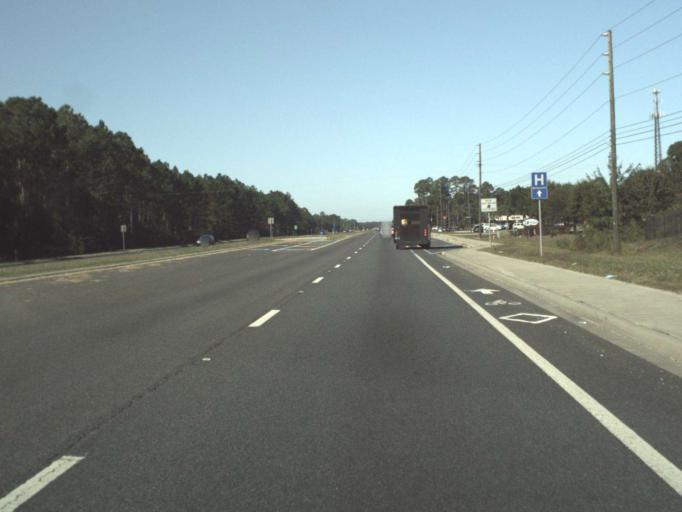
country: US
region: Florida
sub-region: Walton County
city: Seaside
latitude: 30.3744
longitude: -86.2407
